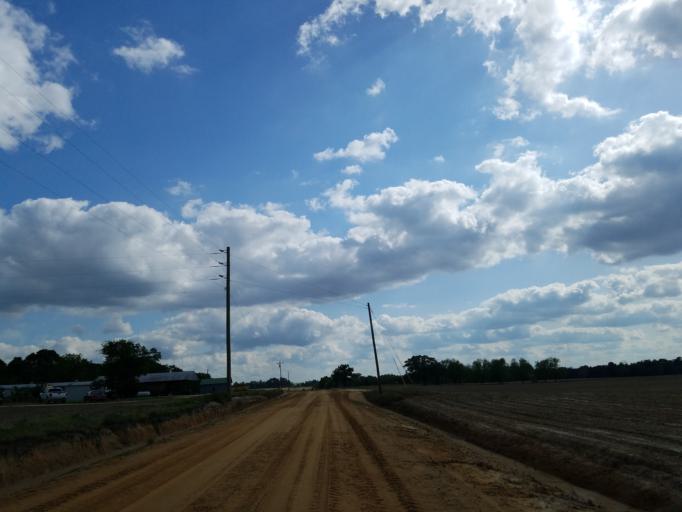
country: US
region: Georgia
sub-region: Dooly County
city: Unadilla
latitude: 32.2312
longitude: -83.7635
